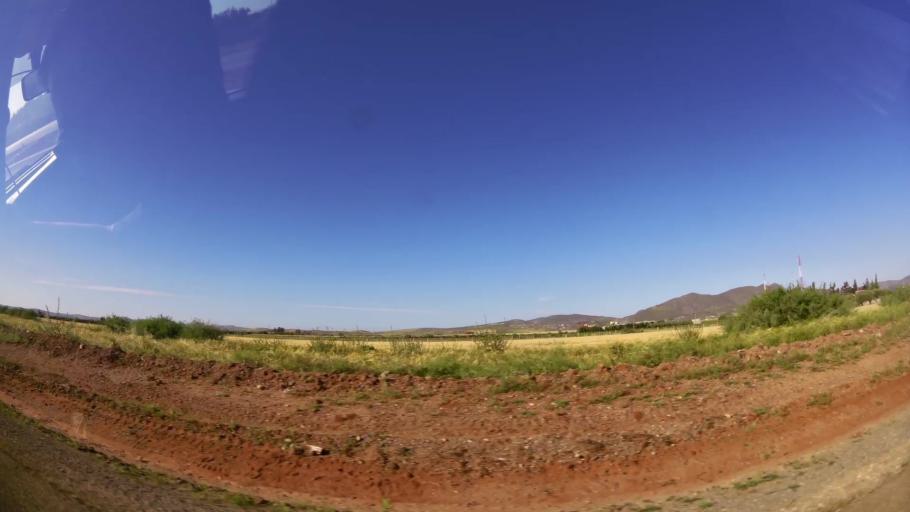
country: MA
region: Oriental
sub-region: Berkane-Taourirt
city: Ahfir
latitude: 34.9878
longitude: -2.1510
